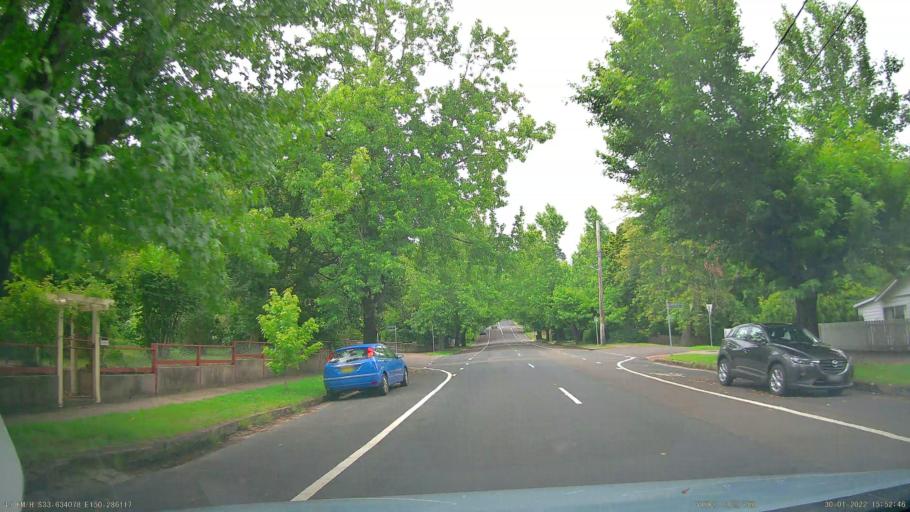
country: AU
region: New South Wales
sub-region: Blue Mountains Municipality
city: Blackheath
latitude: -33.6340
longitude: 150.2861
